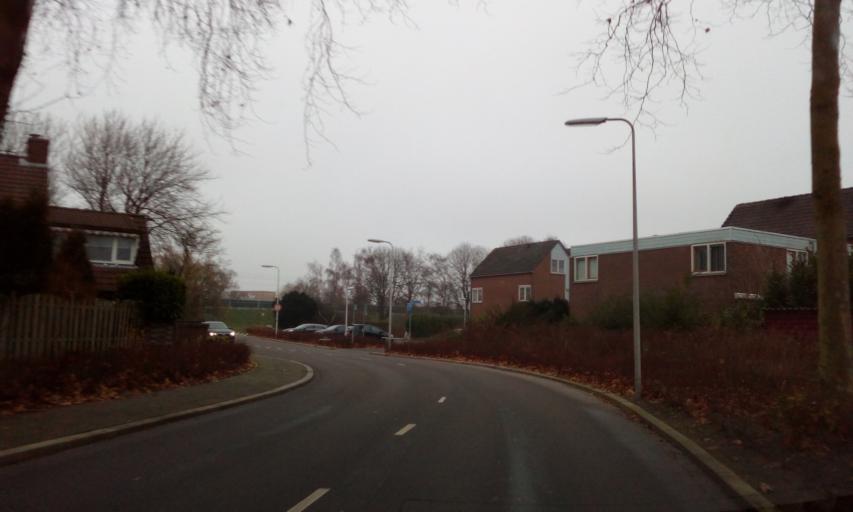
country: NL
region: South Holland
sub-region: Gemeente Capelle aan den IJssel
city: Capelle aan den IJssel
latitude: 51.9519
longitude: 4.5736
